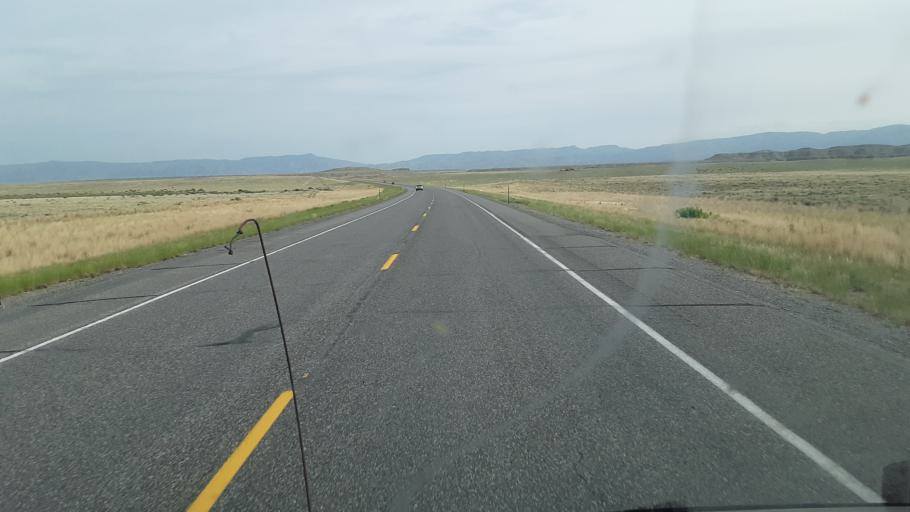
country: US
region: Wyoming
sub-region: Fremont County
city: Riverton
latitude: 43.2592
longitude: -108.1106
